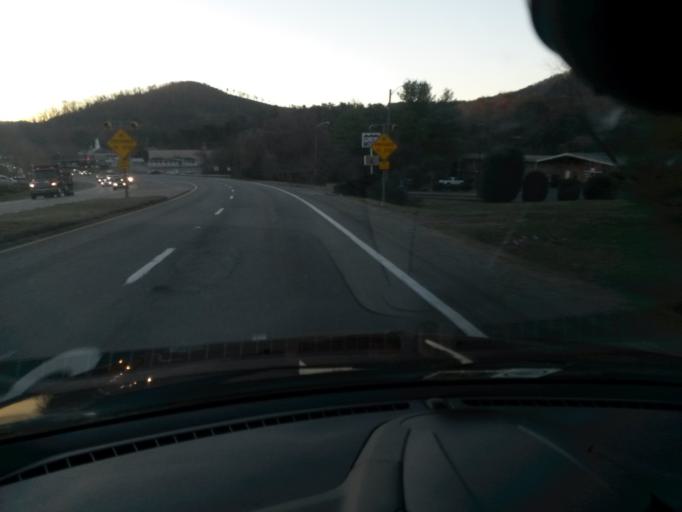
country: US
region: Virginia
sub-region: Roanoke County
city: Narrows
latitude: 37.2067
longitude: -79.9543
